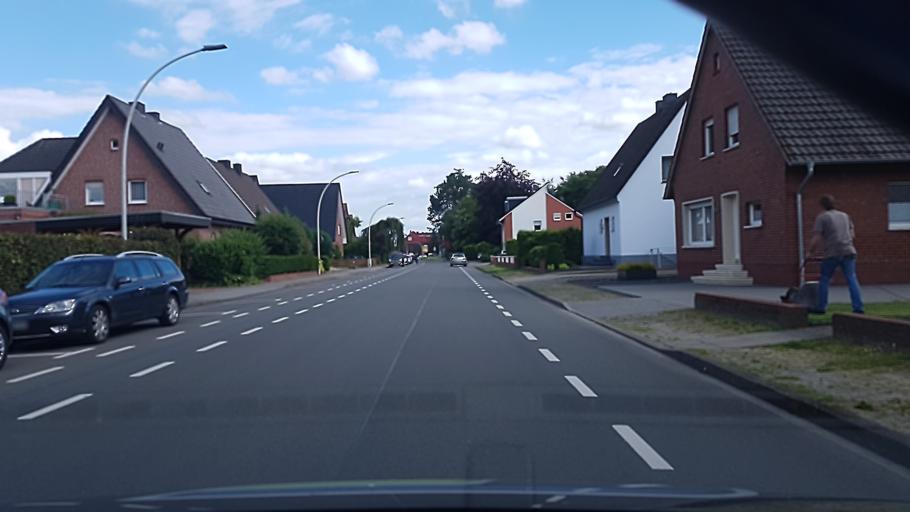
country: DE
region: North Rhine-Westphalia
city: Emsdetten
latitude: 52.1704
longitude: 7.5026
